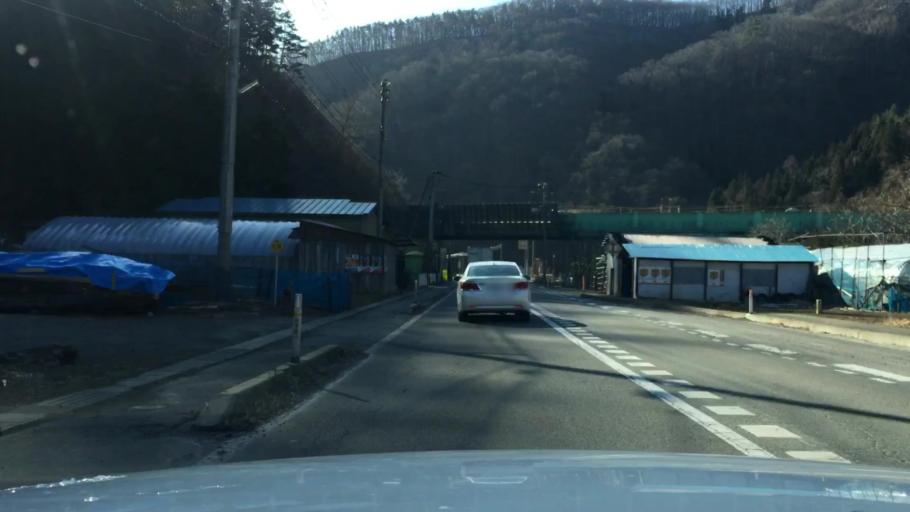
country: JP
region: Iwate
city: Miyako
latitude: 39.6008
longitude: 141.6474
